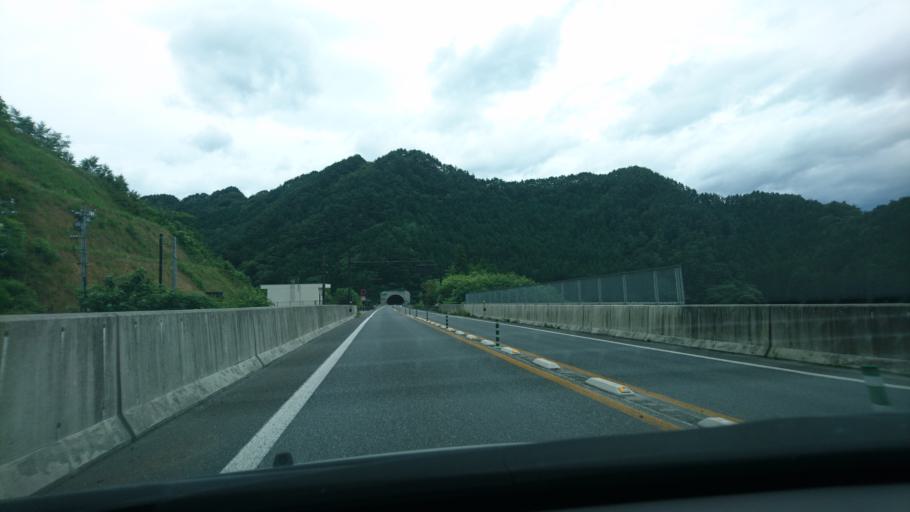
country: JP
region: Iwate
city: Kamaishi
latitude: 39.3217
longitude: 141.8807
